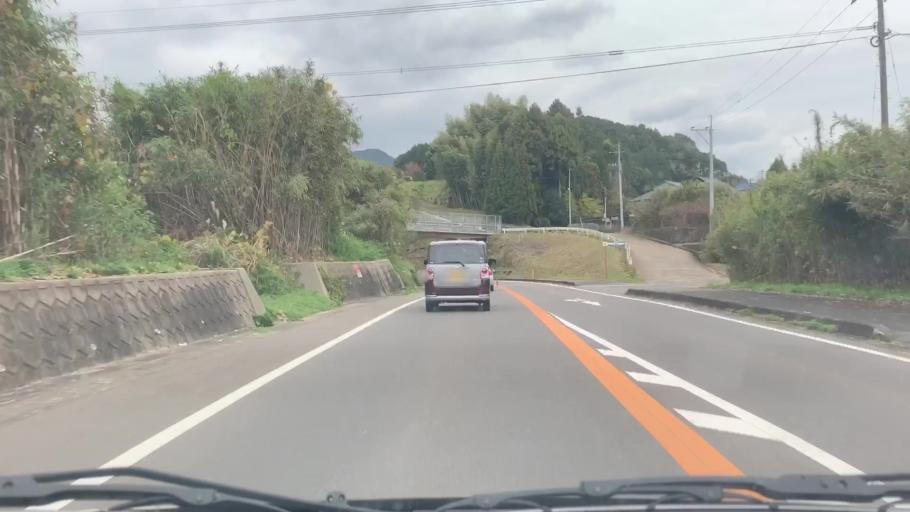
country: JP
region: Saga Prefecture
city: Ureshinomachi-shimojuku
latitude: 33.0882
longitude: 130.0146
